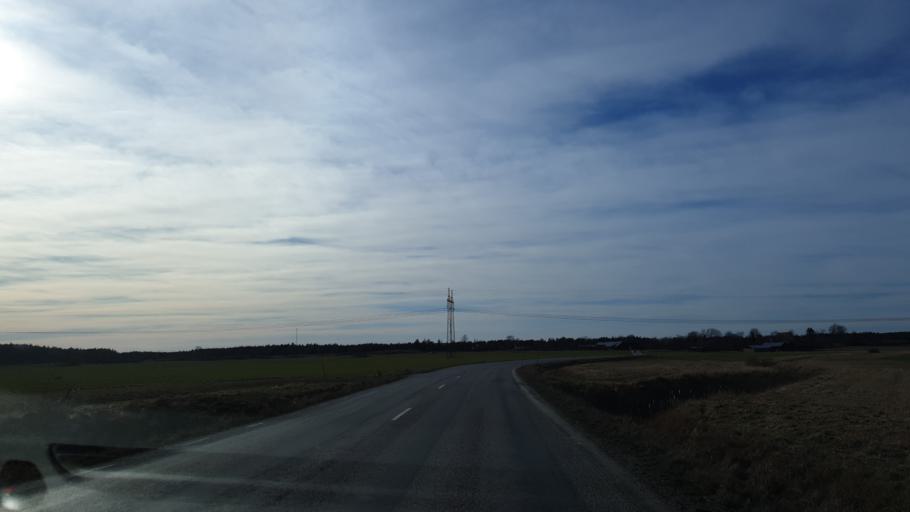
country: SE
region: Uppsala
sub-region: Enkopings Kommun
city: Grillby
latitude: 59.5927
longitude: 17.1935
